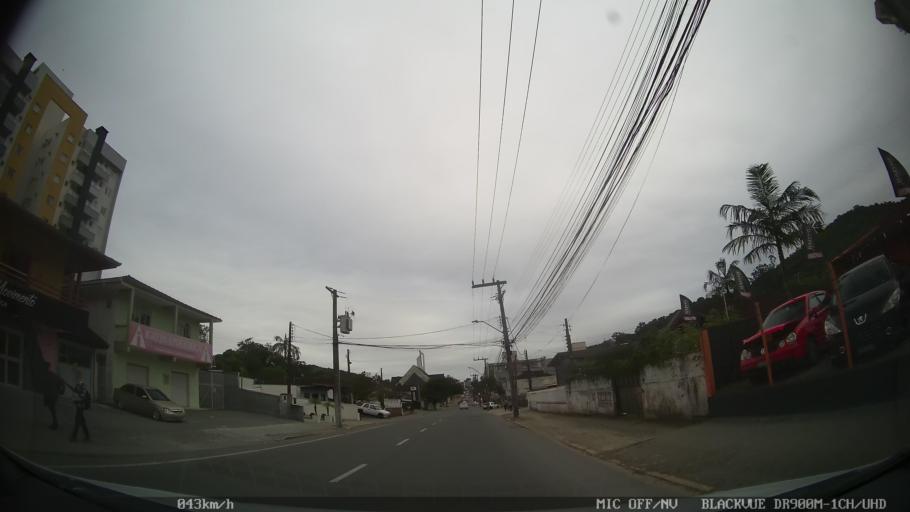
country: BR
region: Santa Catarina
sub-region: Joinville
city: Joinville
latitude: -26.2680
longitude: -48.8231
